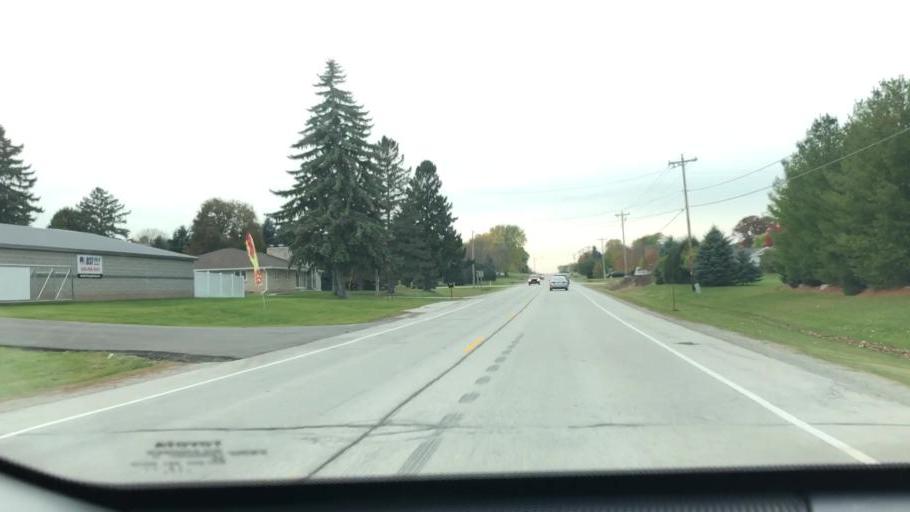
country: US
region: Wisconsin
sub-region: Brown County
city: De Pere
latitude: 44.4452
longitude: -88.1045
